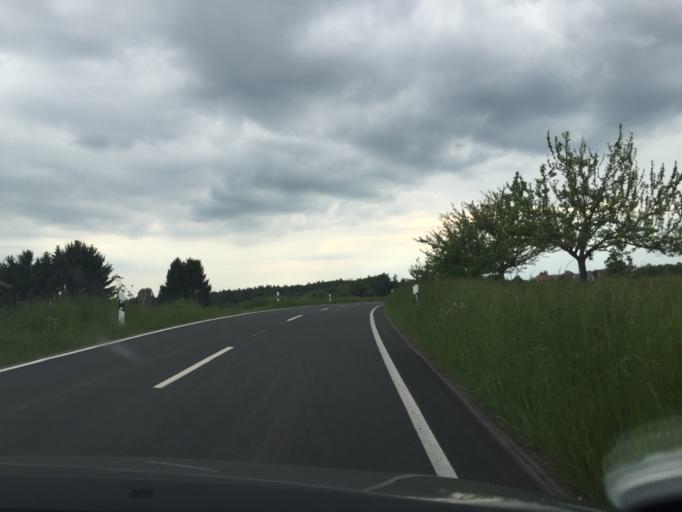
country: DE
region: Bavaria
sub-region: Regierungsbezirk Unterfranken
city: Johannesberg
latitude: 50.0317
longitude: 9.1556
